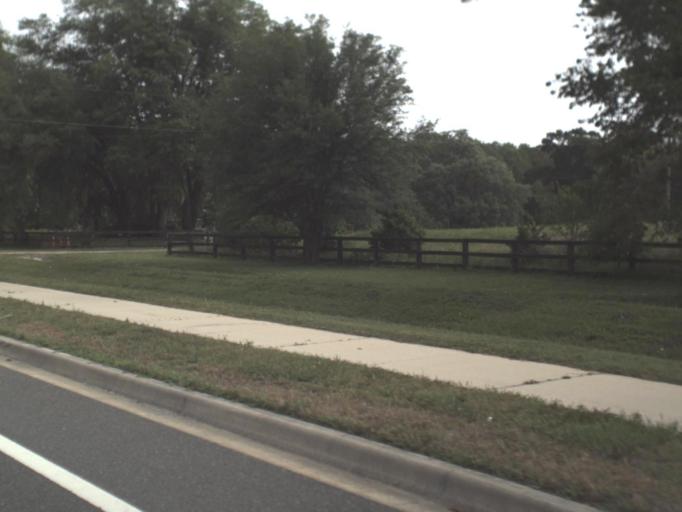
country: US
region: Florida
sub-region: Clay County
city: Green Cove Springs
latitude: 29.9669
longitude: -81.4982
